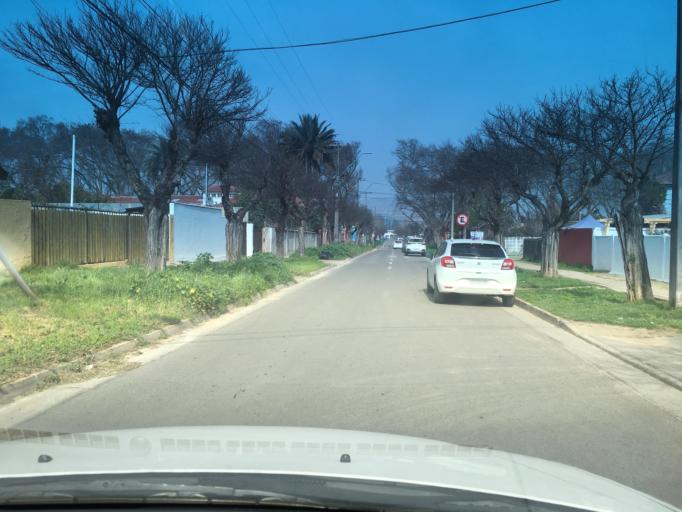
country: CL
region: Valparaiso
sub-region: Provincia de Marga Marga
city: Limache
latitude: -32.9885
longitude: -71.2658
